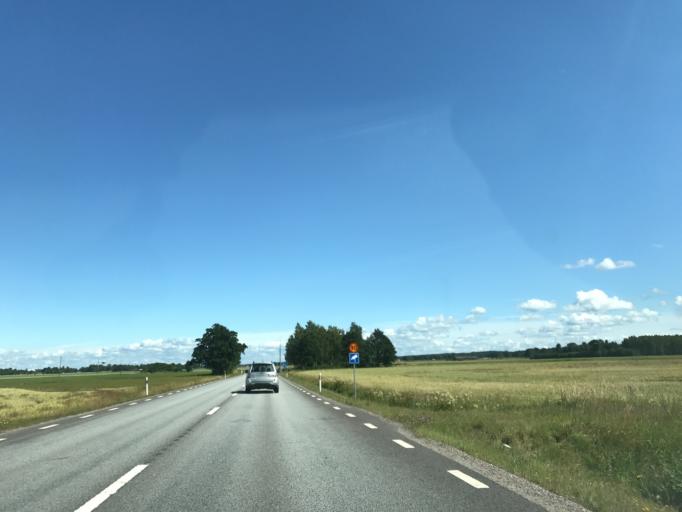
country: SE
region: OErebro
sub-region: Orebro Kommun
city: Odensbacken
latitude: 59.1539
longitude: 15.4778
